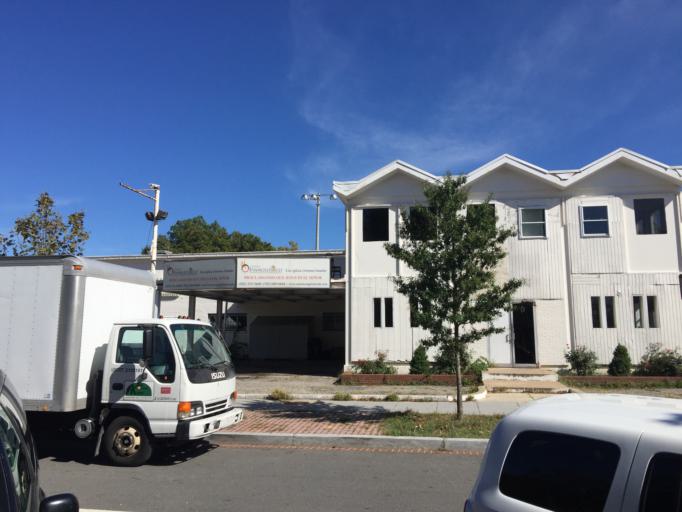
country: US
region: Maryland
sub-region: Montgomery County
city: Takoma Park
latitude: 38.9411
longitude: -77.0251
